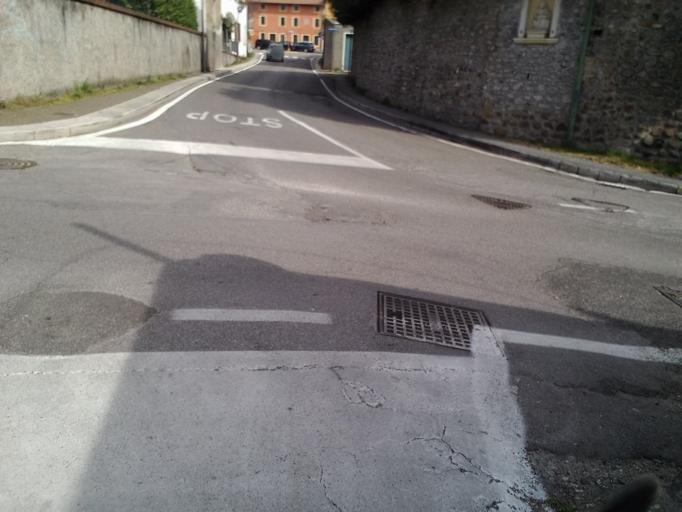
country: IT
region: Veneto
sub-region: Provincia di Verona
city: Sommacampagna
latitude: 45.4060
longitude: 10.8418
